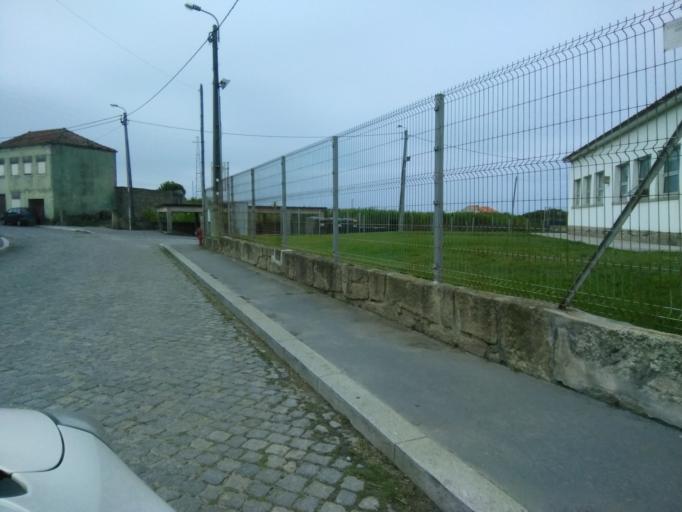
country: PT
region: Porto
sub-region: Matosinhos
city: Lavra
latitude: 41.2353
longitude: -8.7167
